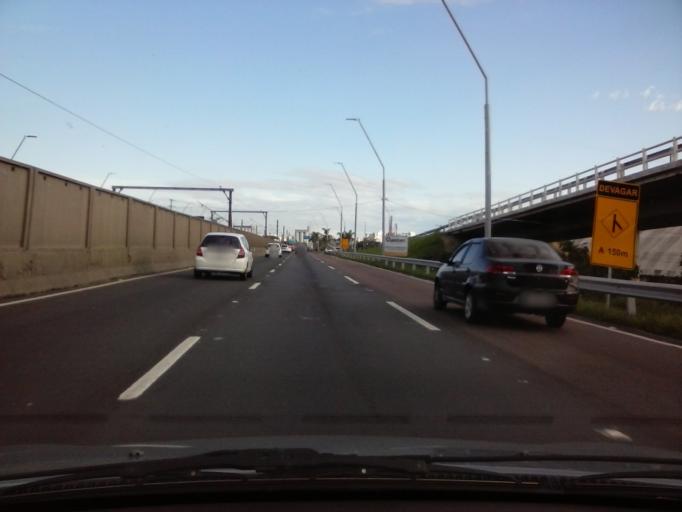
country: BR
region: Rio Grande do Sul
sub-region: Porto Alegre
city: Porto Alegre
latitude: -30.0000
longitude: -51.2073
